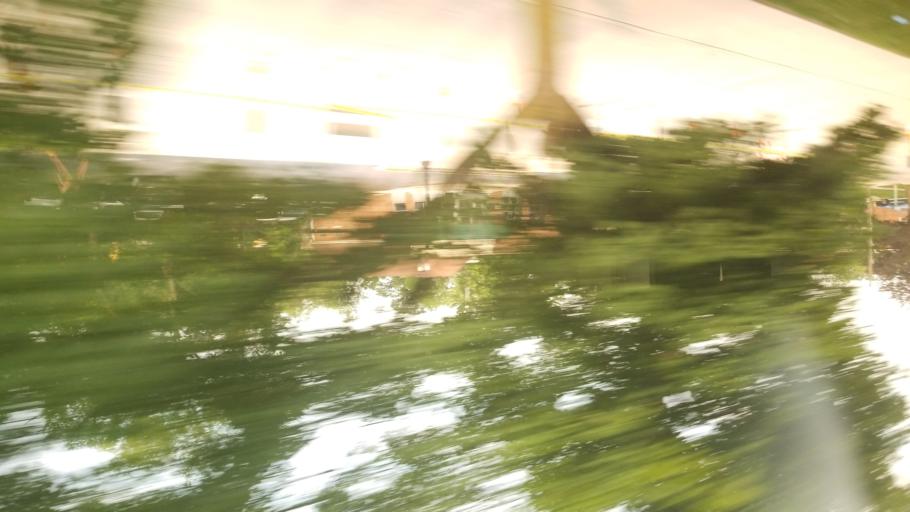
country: US
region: Illinois
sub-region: Cook County
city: Western Springs
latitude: 41.8097
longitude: -87.8984
